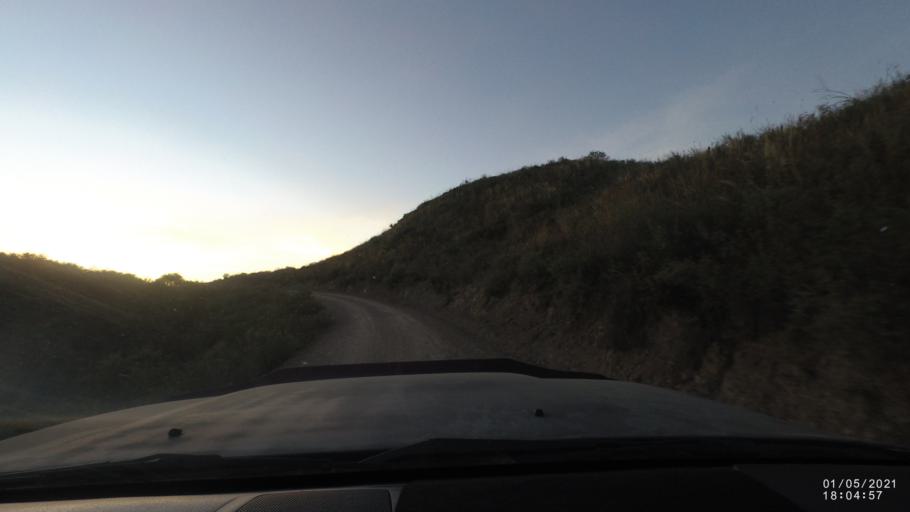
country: BO
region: Cochabamba
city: Capinota
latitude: -17.6884
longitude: -66.1805
